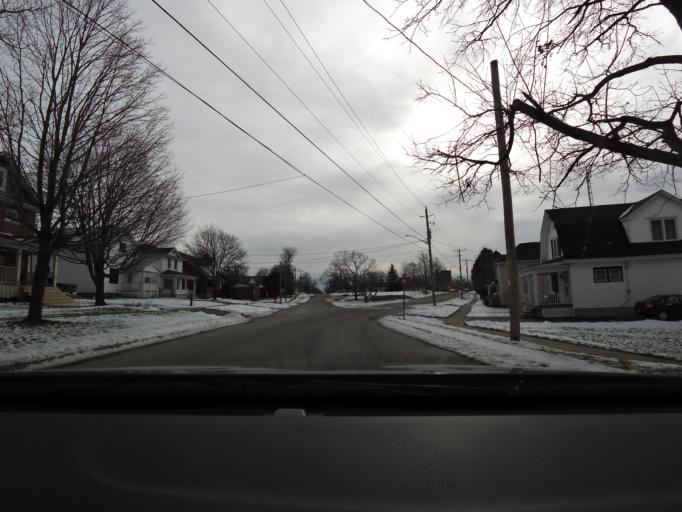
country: CA
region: Ontario
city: Ancaster
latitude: 42.9524
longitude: -79.8584
